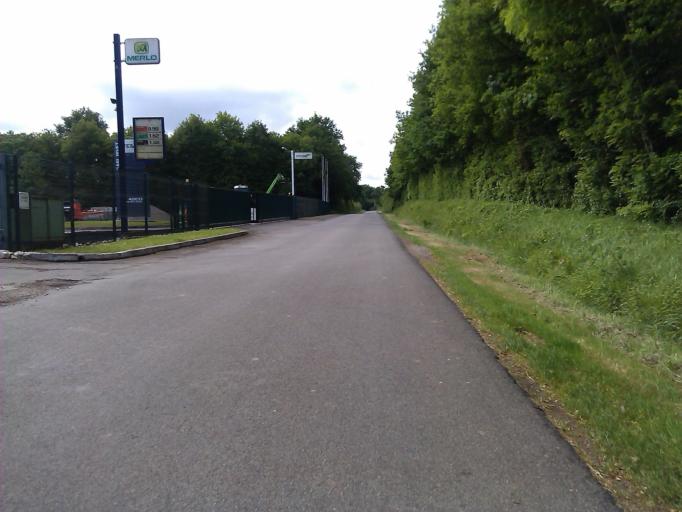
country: FR
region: Poitou-Charentes
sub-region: Departement de la Charente
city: Champagne-Mouton
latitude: 46.0270
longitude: 0.4449
